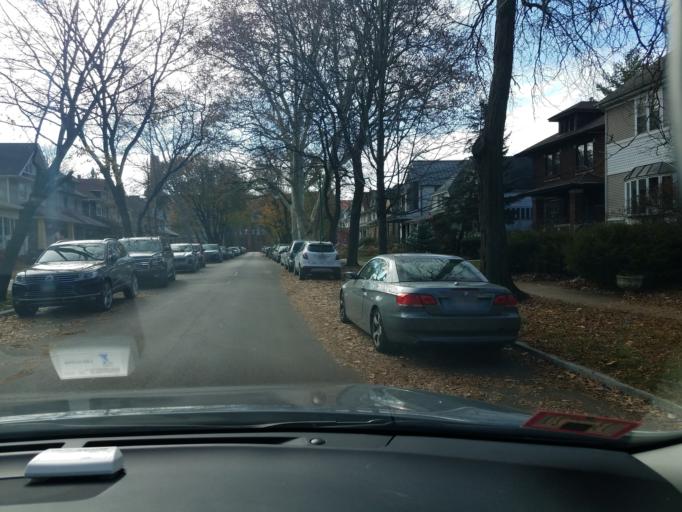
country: US
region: Illinois
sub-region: Cook County
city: Lincolnwood
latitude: 41.9498
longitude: -87.7353
